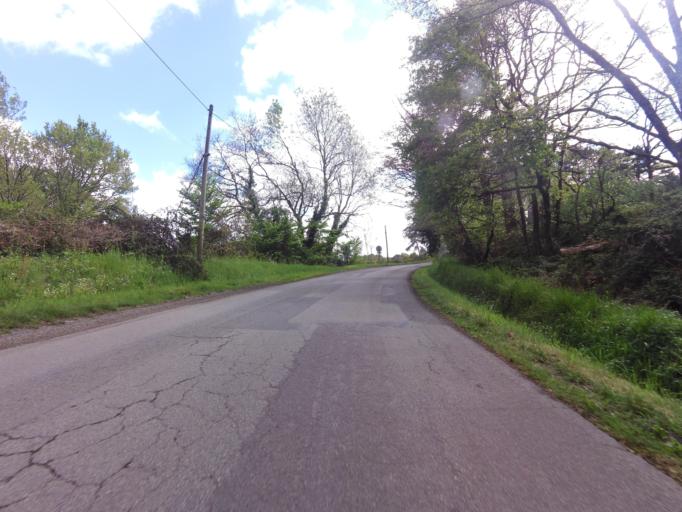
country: FR
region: Brittany
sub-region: Departement du Morbihan
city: Plougoumelen
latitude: 47.6447
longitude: -2.9232
